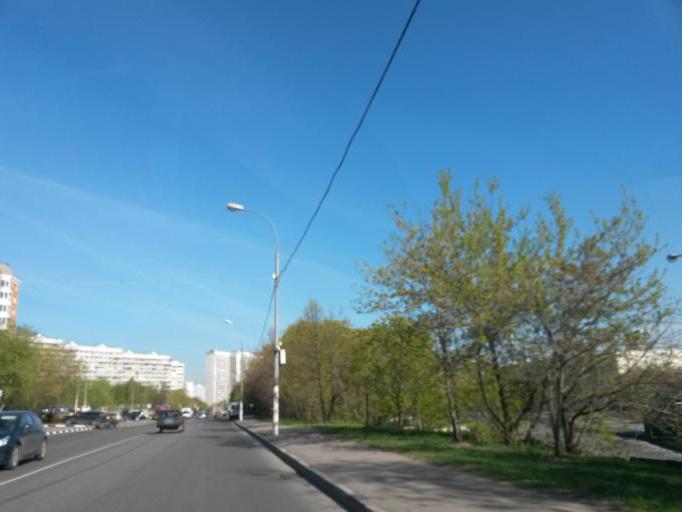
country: RU
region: Moscow
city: Zyablikovo
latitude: 55.6232
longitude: 37.7561
